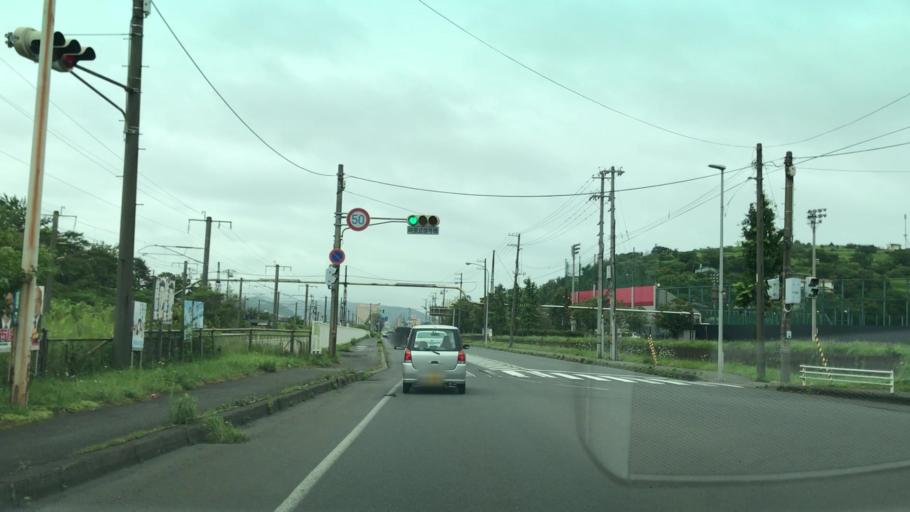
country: JP
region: Hokkaido
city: Muroran
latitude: 42.3383
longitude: 141.0146
